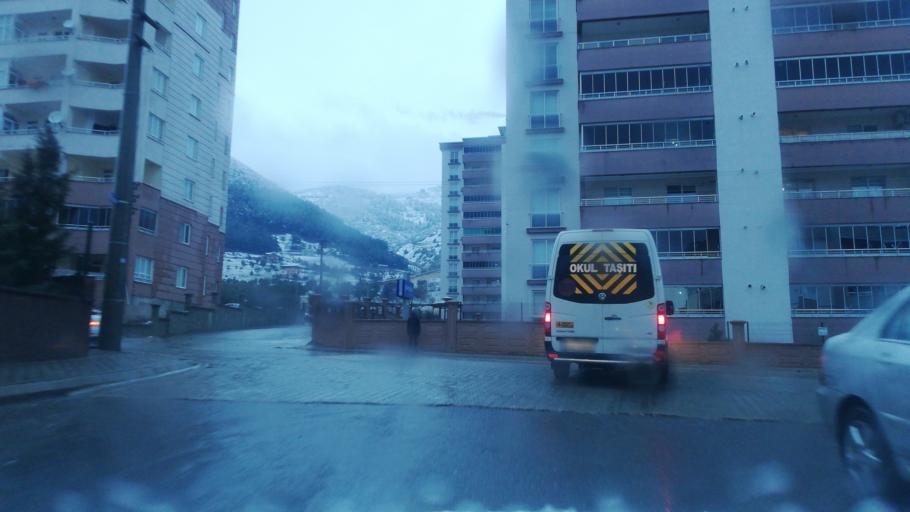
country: TR
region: Kahramanmaras
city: Kahramanmaras
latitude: 37.6004
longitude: 36.8823
